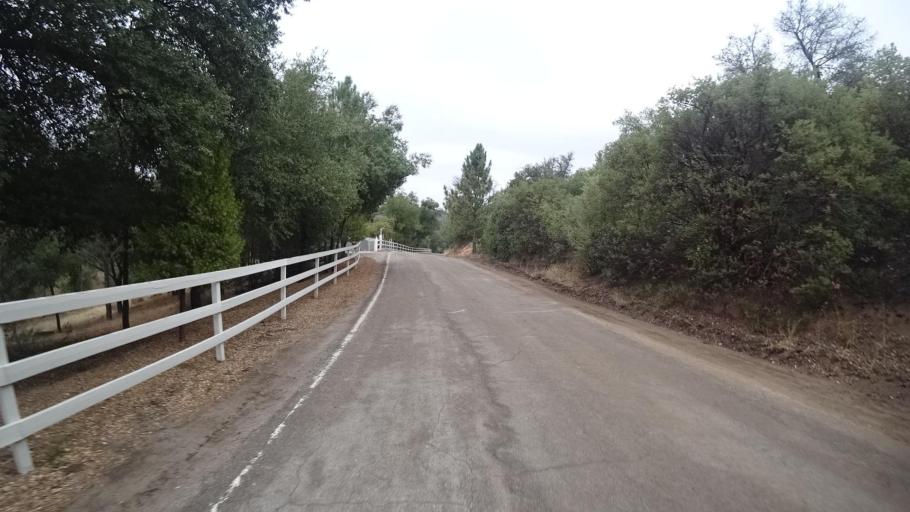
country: US
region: California
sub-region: San Diego County
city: Julian
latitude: 33.0192
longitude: -116.6353
